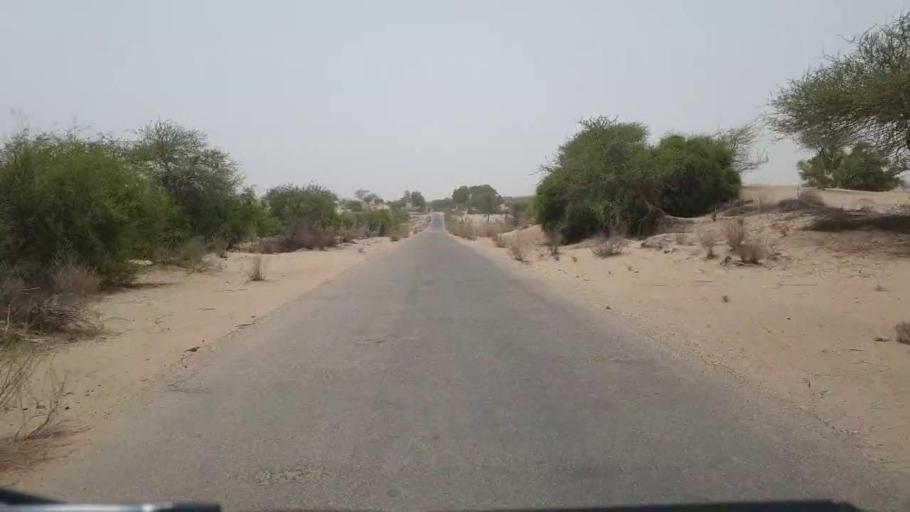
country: PK
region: Sindh
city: Naukot
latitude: 24.7821
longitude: 69.5334
